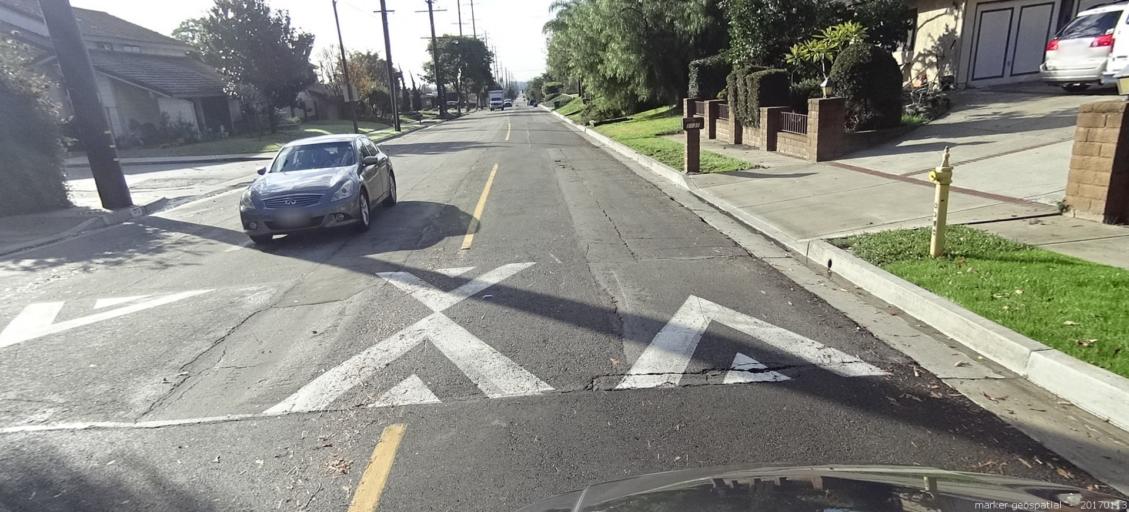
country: US
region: California
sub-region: Orange County
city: La Habra
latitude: 33.9417
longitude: -117.9244
